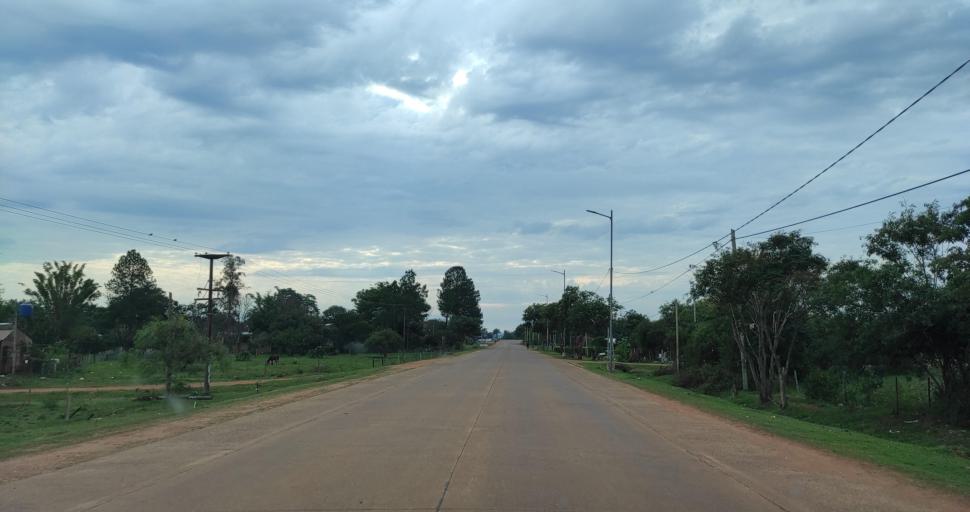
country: AR
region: Corrientes
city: Santo Tome
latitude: -28.5499
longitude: -56.0655
